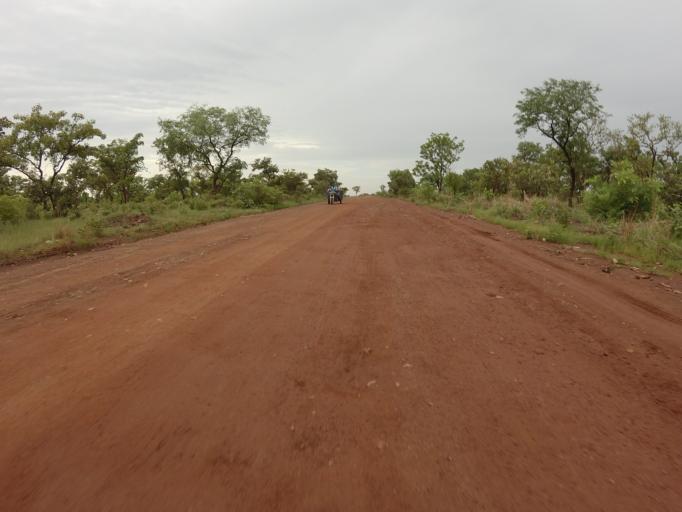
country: GH
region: Upper East
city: Bolgatanga
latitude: 10.8781
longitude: -0.6290
